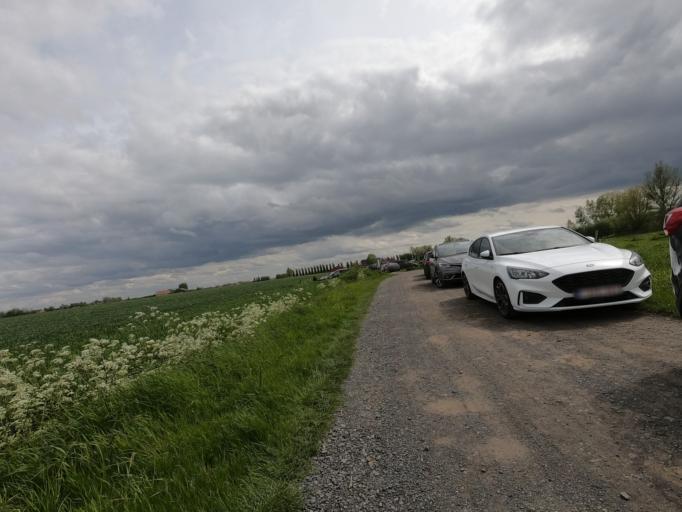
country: BE
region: Flanders
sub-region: Provincie West-Vlaanderen
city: Alveringem
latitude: 50.9411
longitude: 2.7540
